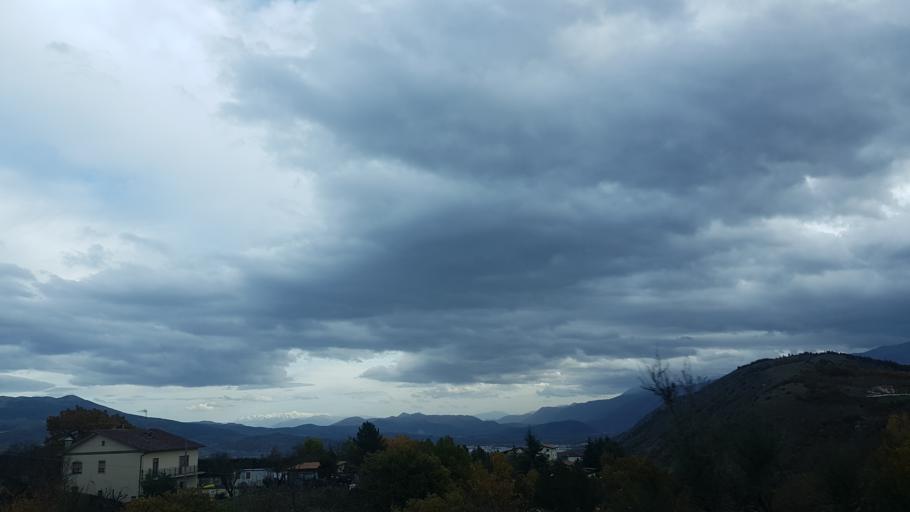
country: IT
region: Abruzzo
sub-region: Provincia dell' Aquila
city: L'Aquila
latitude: 42.3654
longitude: 13.4284
